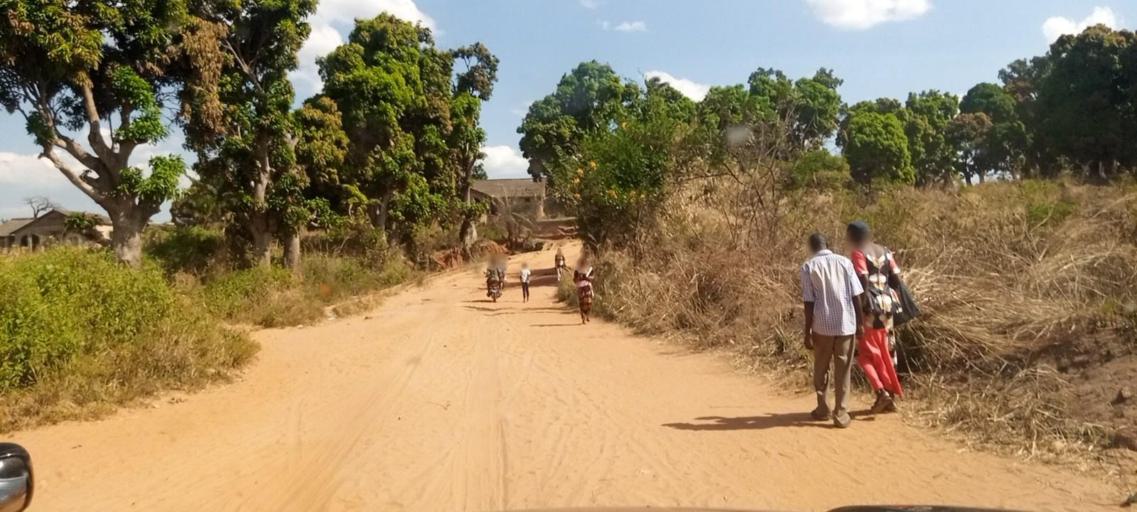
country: CD
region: Kasai-Oriental
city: Kabinda
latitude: -6.1294
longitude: 24.4956
